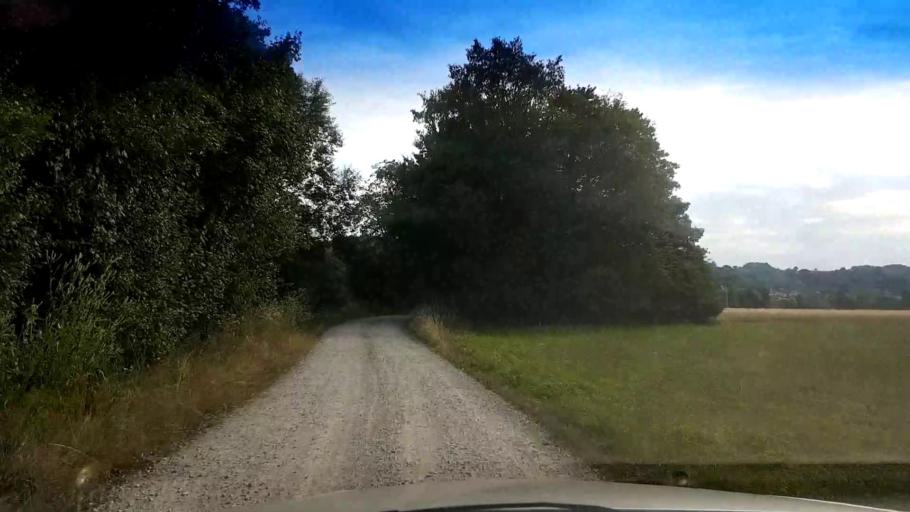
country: DE
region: Bavaria
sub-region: Regierungsbezirk Unterfranken
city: Ebelsbach
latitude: 49.9744
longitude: 10.6803
